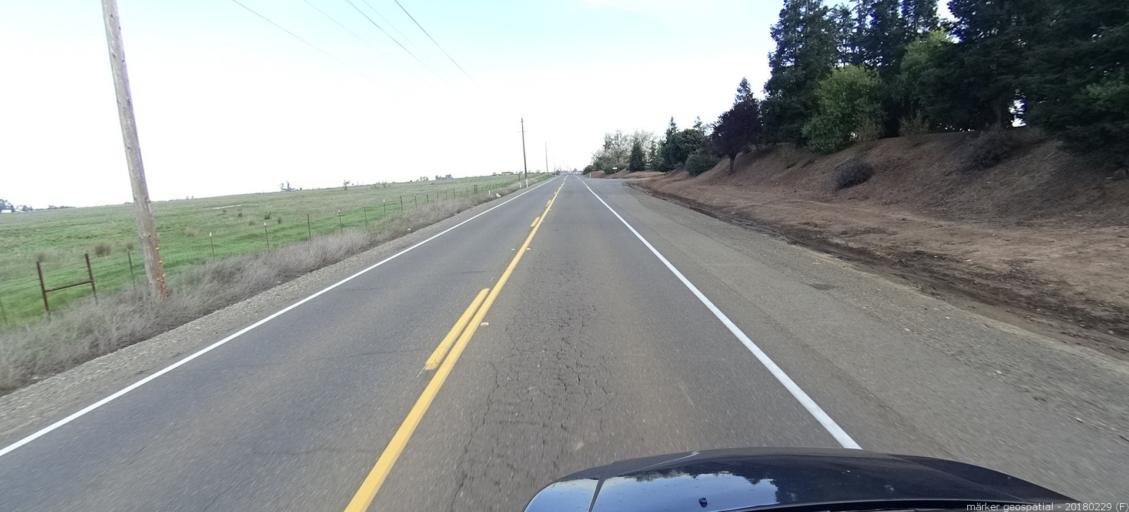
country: US
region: California
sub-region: Sacramento County
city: Vineyard
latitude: 38.4860
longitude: -121.2977
